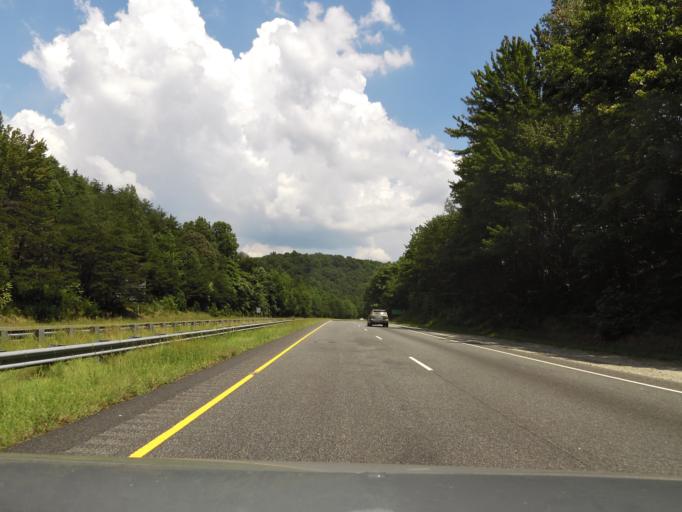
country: US
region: North Carolina
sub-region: Polk County
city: Columbus
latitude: 35.2571
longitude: -82.1967
